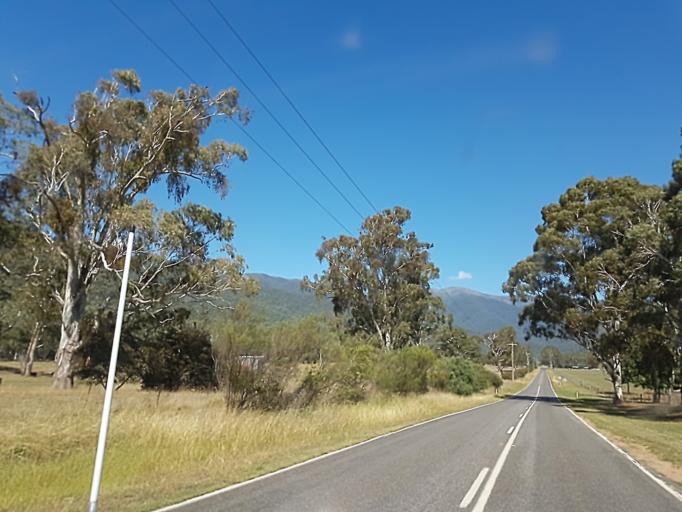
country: AU
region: Victoria
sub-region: Alpine
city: Mount Beauty
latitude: -36.8204
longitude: 147.0654
